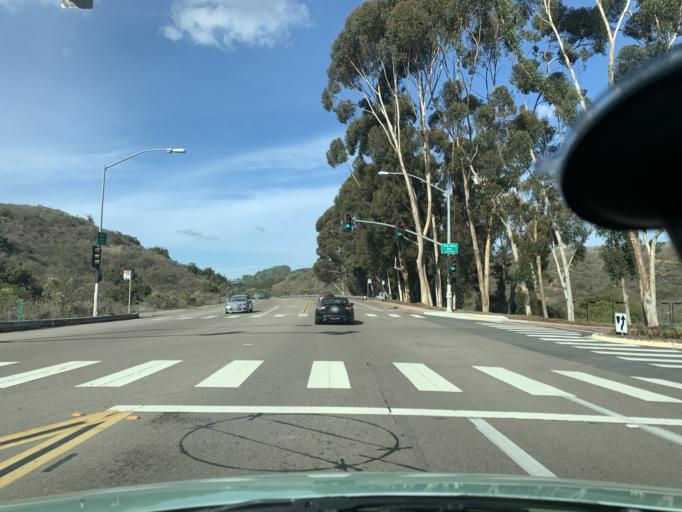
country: US
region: California
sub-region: San Diego County
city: San Diego
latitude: 32.7974
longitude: -117.1717
